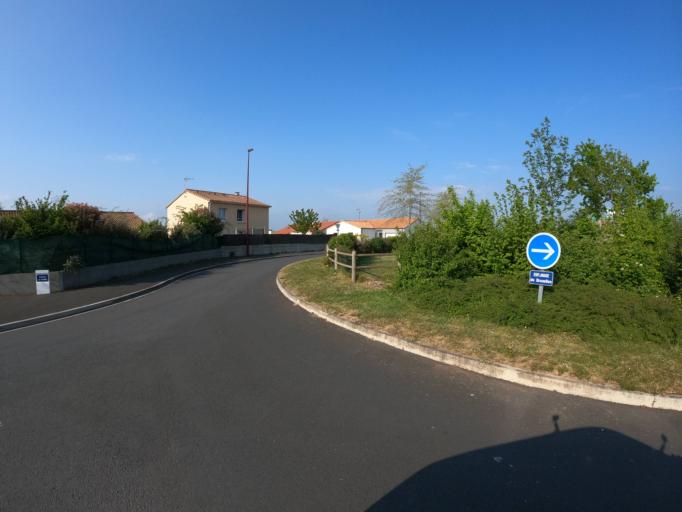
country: FR
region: Pays de la Loire
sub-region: Departement de Maine-et-Loire
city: La Seguiniere
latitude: 47.0671
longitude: -0.9514
